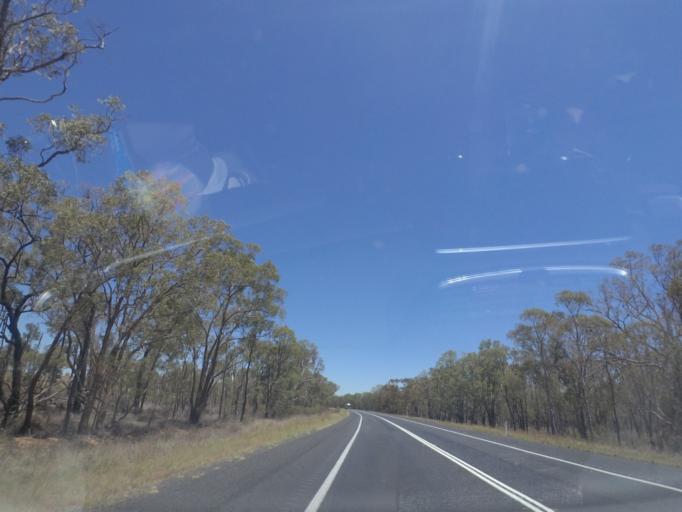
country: AU
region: New South Wales
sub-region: Warrumbungle Shire
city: Coonabarabran
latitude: -31.2075
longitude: 149.3325
